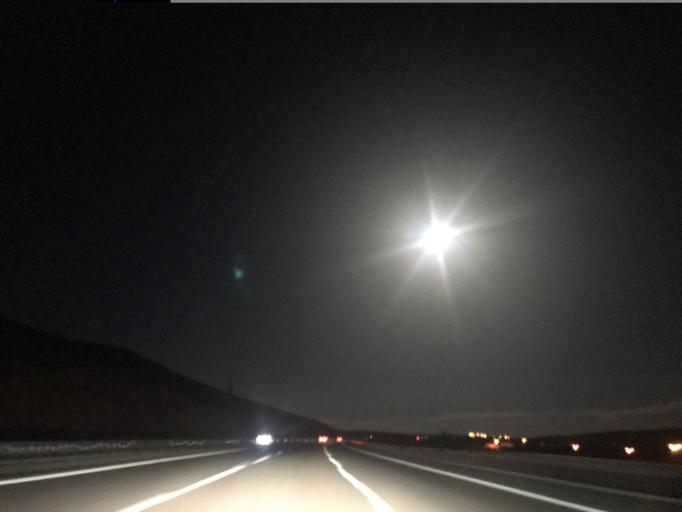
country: TR
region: Nigde
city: Ulukisla
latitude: 37.6350
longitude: 34.4891
